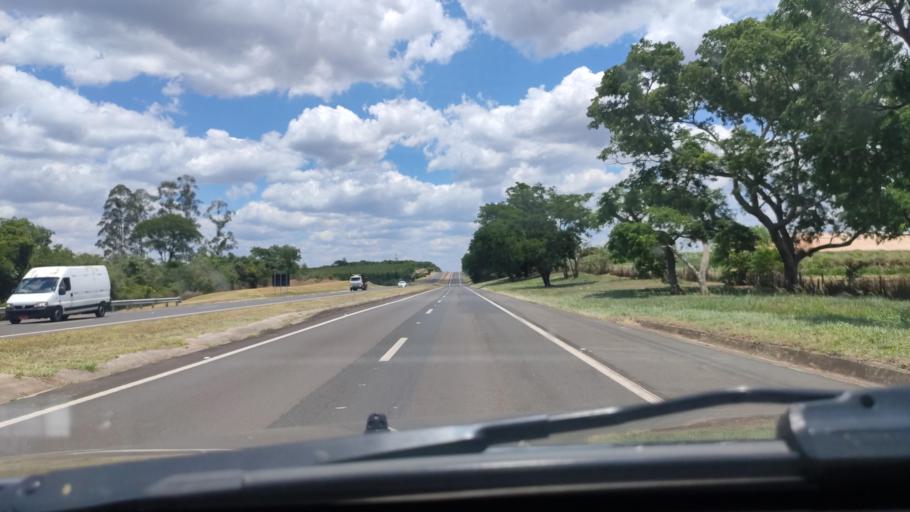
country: BR
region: Sao Paulo
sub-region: Duartina
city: Duartina
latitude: -22.5050
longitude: -49.2864
